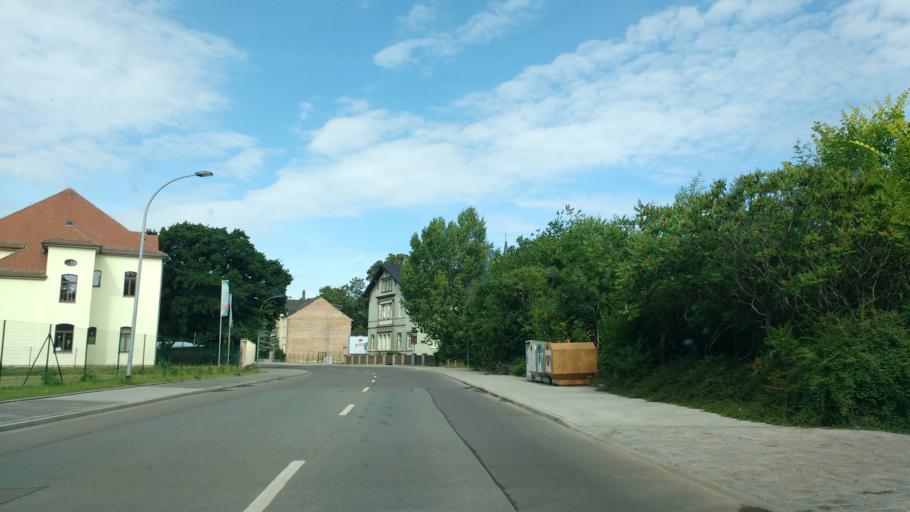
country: DE
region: Saxony-Anhalt
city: Zeitz
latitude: 51.0534
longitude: 12.1332
